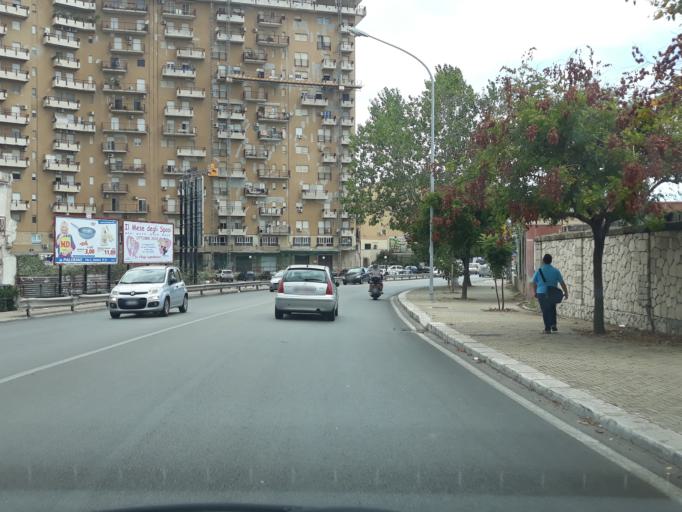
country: IT
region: Sicily
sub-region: Palermo
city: Ciaculli
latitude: 38.1104
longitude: 13.3787
